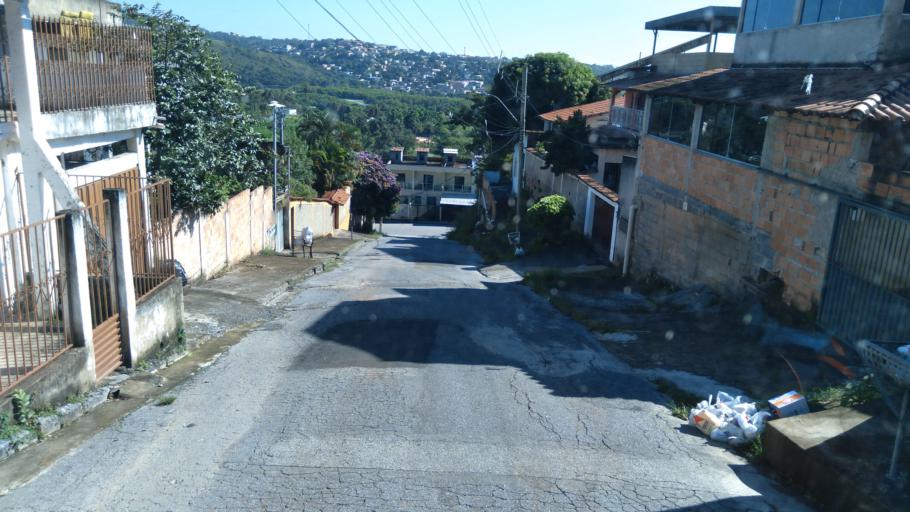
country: BR
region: Minas Gerais
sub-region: Santa Luzia
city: Santa Luzia
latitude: -19.8278
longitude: -43.8975
